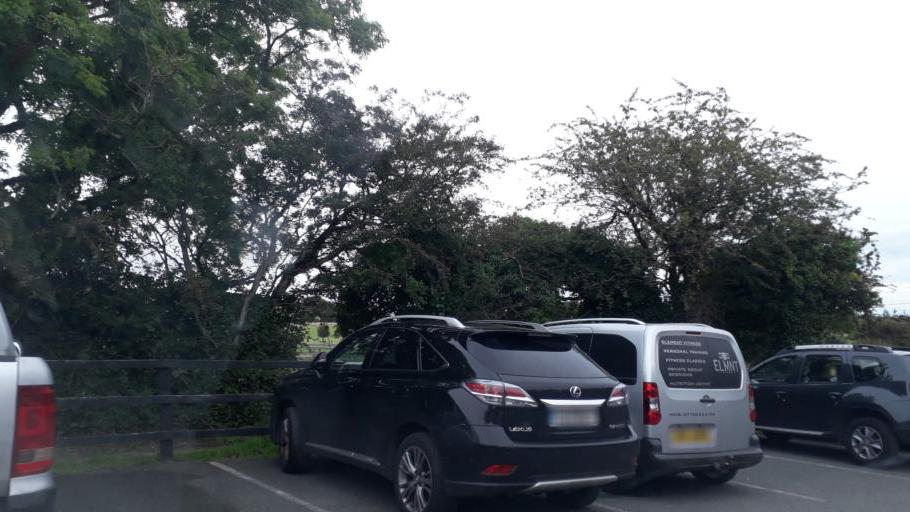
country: IE
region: Leinster
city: Sandyford
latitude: 53.2229
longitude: -6.2248
